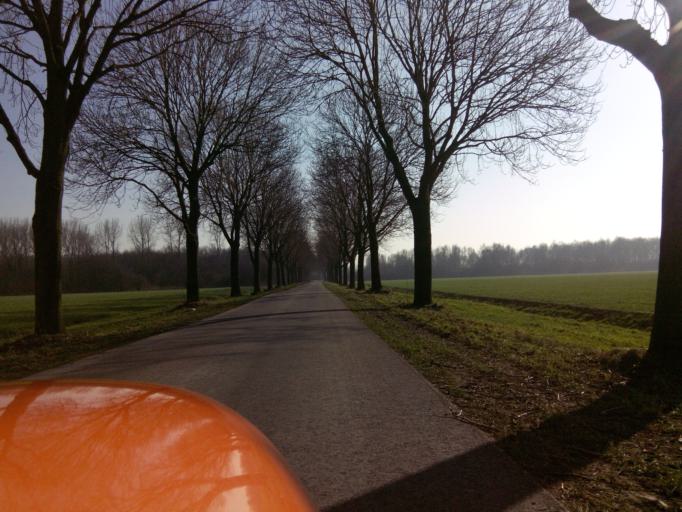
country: NL
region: Gelderland
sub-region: Gemeente Nijkerk
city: Nijkerk
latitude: 52.2719
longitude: 5.4802
